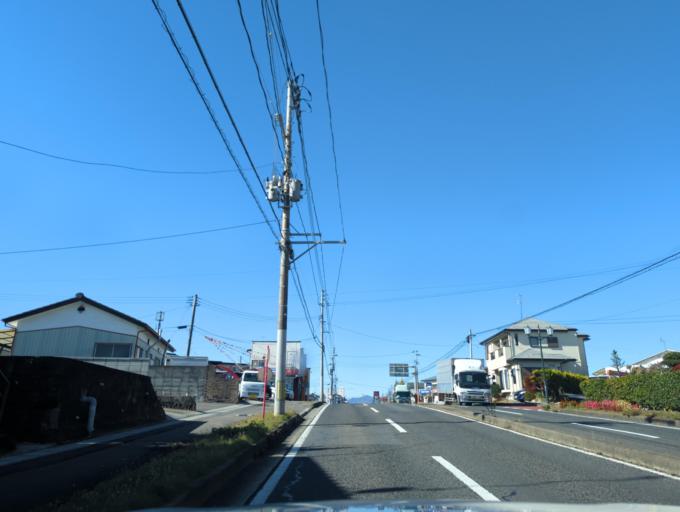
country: JP
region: Fukushima
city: Koriyama
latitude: 37.4265
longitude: 140.3899
